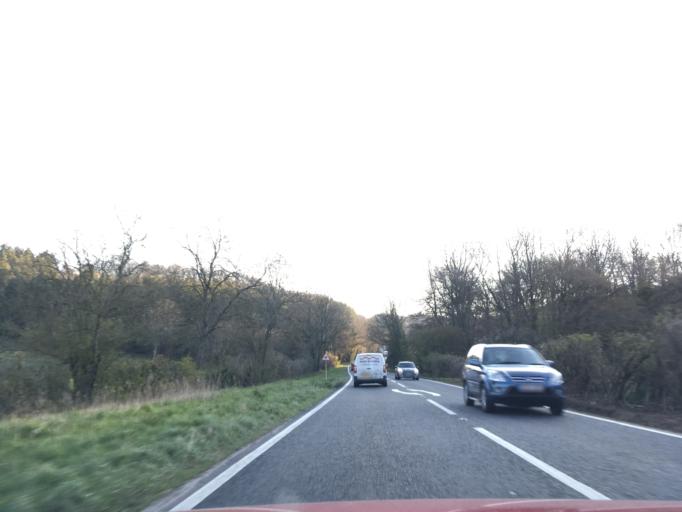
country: GB
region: England
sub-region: Gloucestershire
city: Charlton Kings
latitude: 51.8559
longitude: -2.0420
